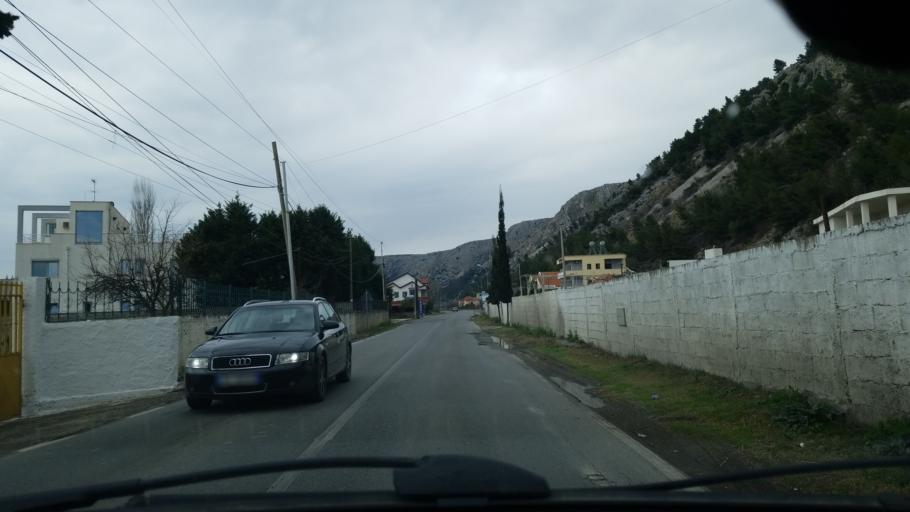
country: AL
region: Lezhe
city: Lezhe
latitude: 41.7906
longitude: 19.6242
